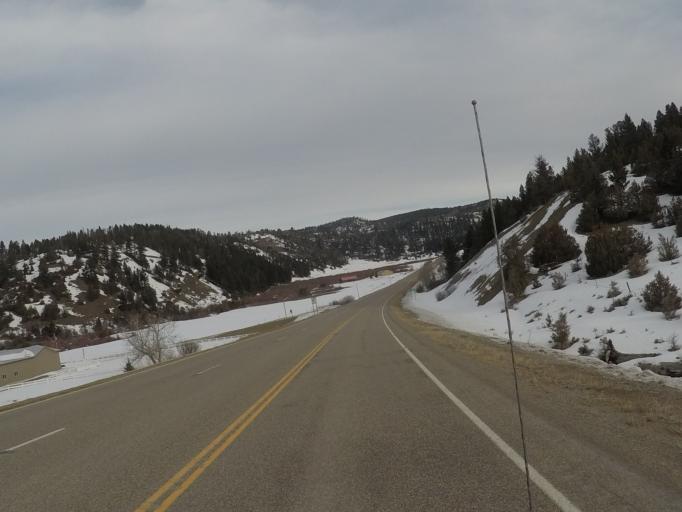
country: US
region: Montana
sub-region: Meagher County
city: White Sulphur Springs
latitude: 46.6677
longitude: -110.8771
